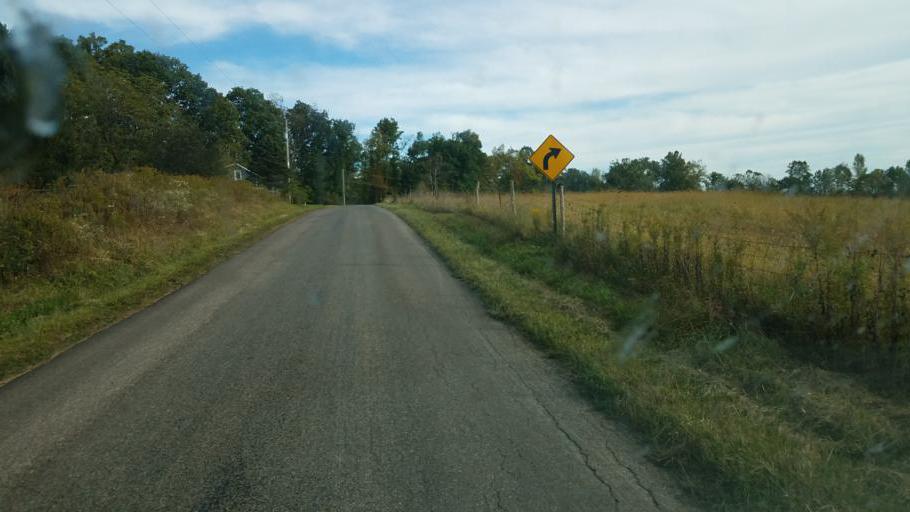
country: US
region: Ohio
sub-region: Knox County
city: Fredericktown
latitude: 40.5495
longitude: -82.5966
